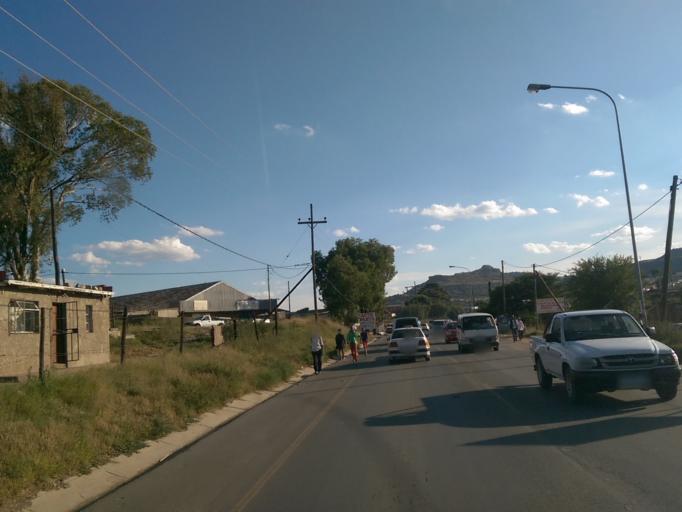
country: LS
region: Maseru
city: Maseru
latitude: -29.3095
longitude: 27.5131
